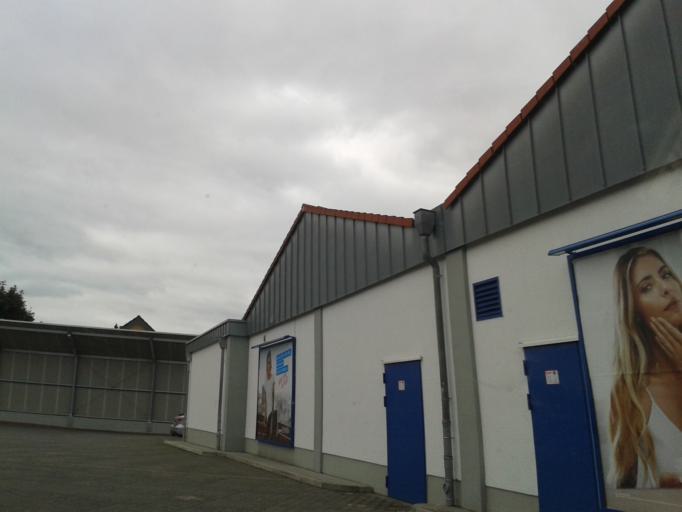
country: DE
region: North Rhine-Westphalia
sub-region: Regierungsbezirk Detmold
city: Paderborn
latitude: 51.7289
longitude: 8.7309
